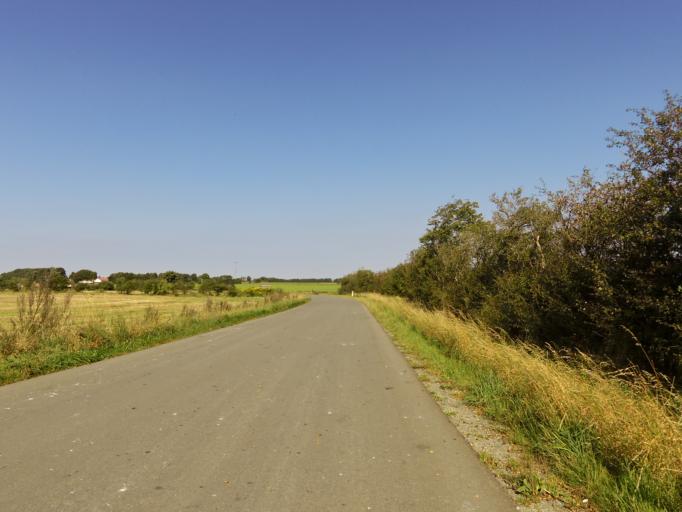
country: DK
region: South Denmark
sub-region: Vejen Kommune
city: Rodding
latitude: 55.3354
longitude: 9.1355
